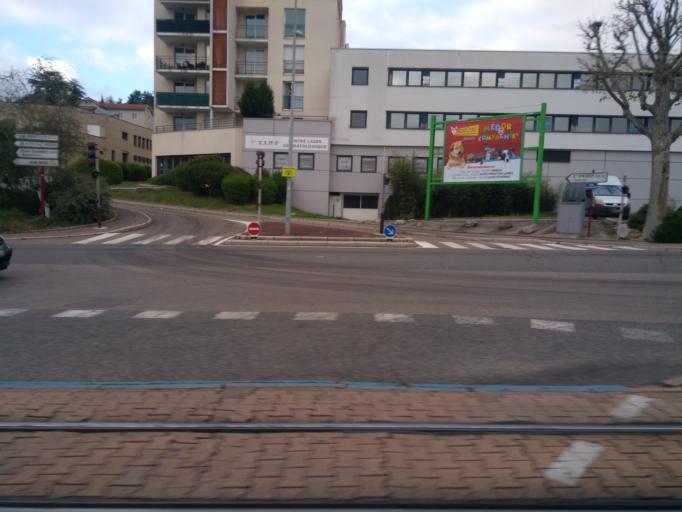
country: FR
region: Rhone-Alpes
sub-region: Departement de la Loire
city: Saint-Priest-en-Jarez
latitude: 45.4713
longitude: 4.3732
